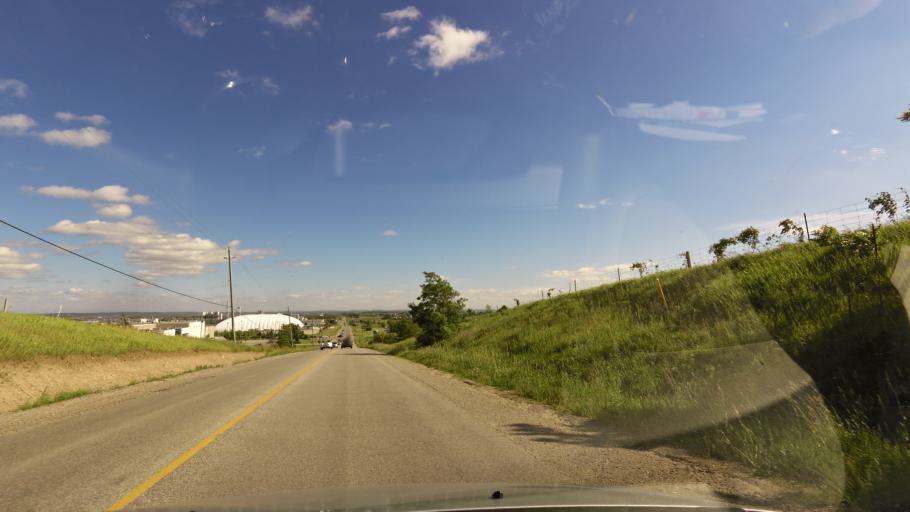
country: CA
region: Ontario
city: Bradford West Gwillimbury
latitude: 44.1212
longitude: -79.6059
